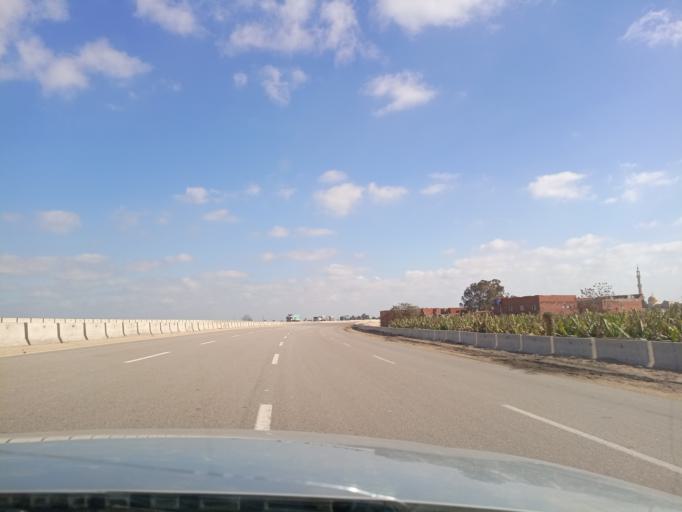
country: EG
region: Muhafazat al Minufiyah
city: Ashmun
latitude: 30.3316
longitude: 30.8375
